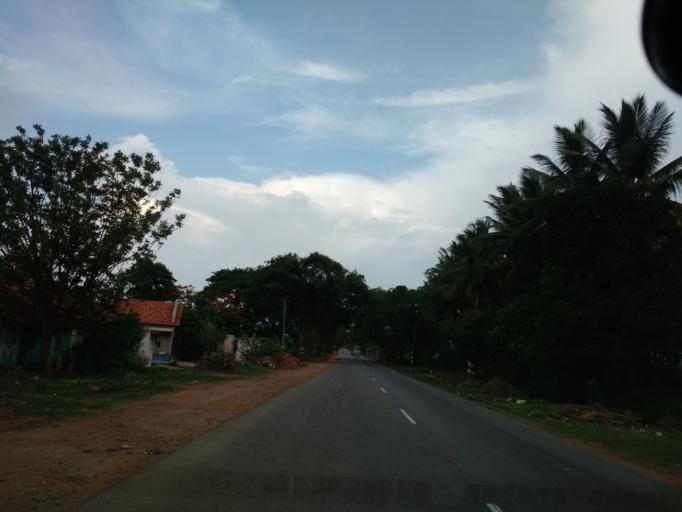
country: IN
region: Karnataka
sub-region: Hassan
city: Banavar
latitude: 13.4768
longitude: 76.1031
